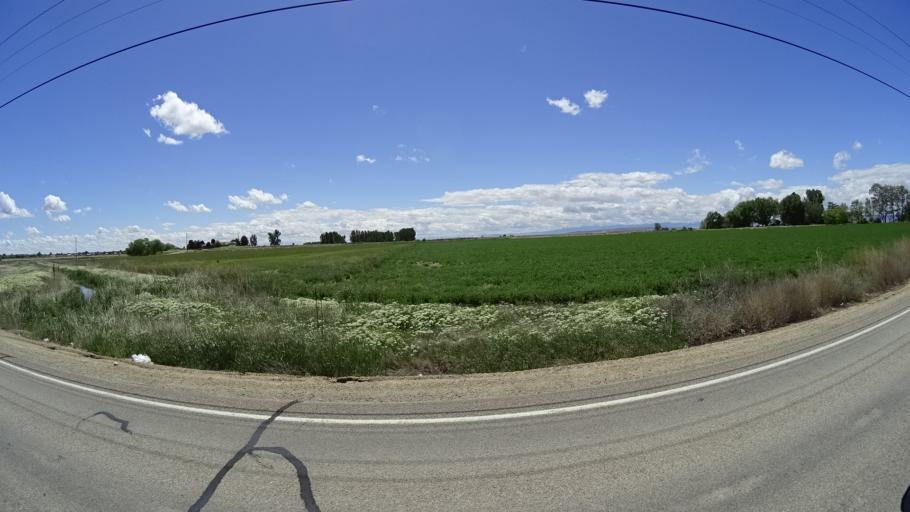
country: US
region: Idaho
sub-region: Ada County
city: Meridian
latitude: 43.5466
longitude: -116.3812
